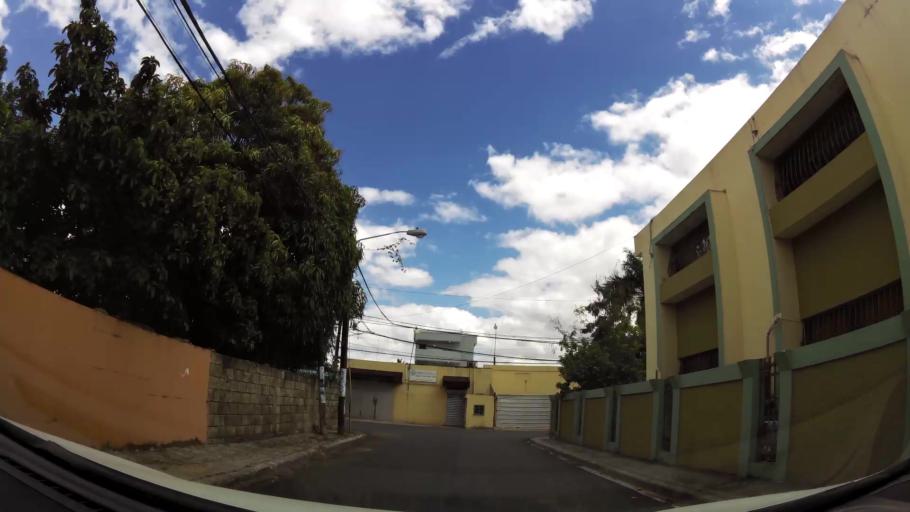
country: DO
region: Nacional
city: Ensanche Luperon
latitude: 18.5261
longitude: -69.9096
